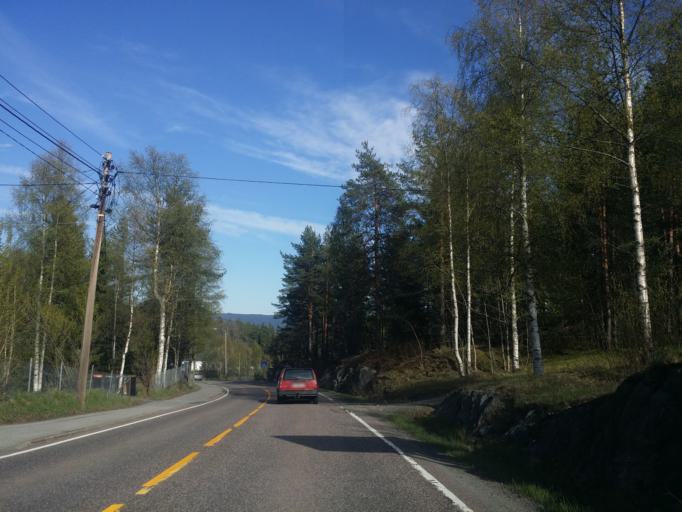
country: NO
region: Buskerud
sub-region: Kongsberg
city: Kongsberg
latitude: 59.6249
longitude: 9.6003
